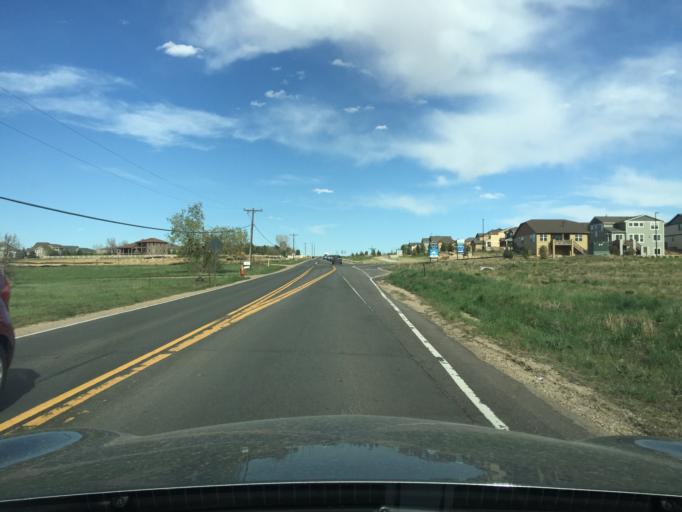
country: US
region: Colorado
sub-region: Boulder County
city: Erie
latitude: 40.0365
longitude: -105.0875
